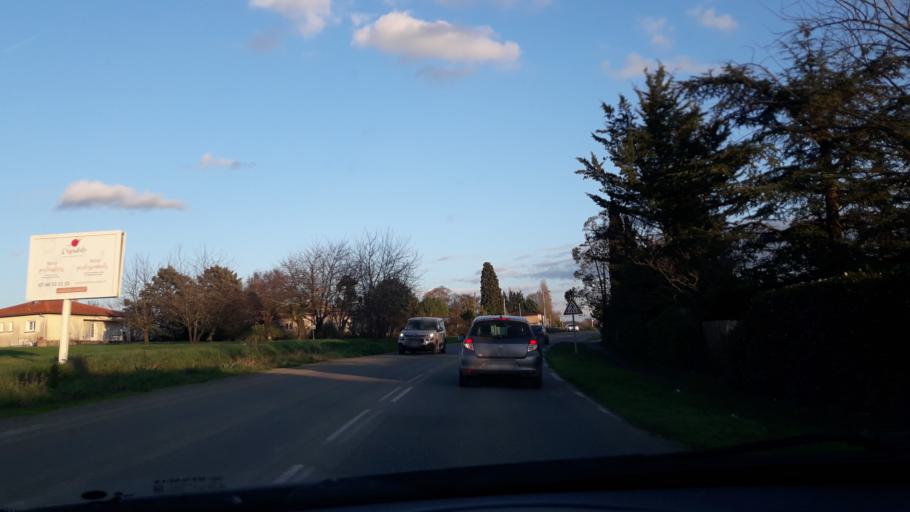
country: FR
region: Midi-Pyrenees
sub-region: Departement du Gers
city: Pujaudran
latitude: 43.6117
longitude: 1.0970
